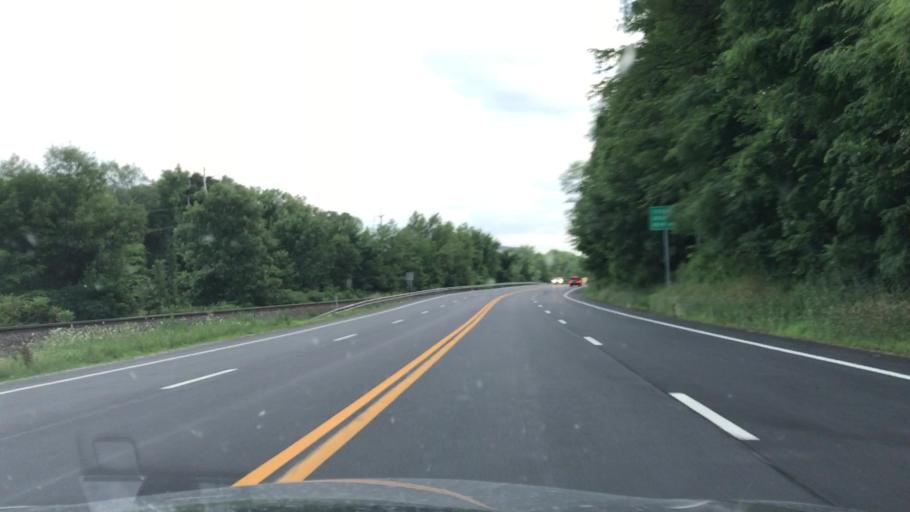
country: US
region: New York
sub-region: Rockland County
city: Sloatsburg
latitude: 41.2337
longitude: -74.1803
